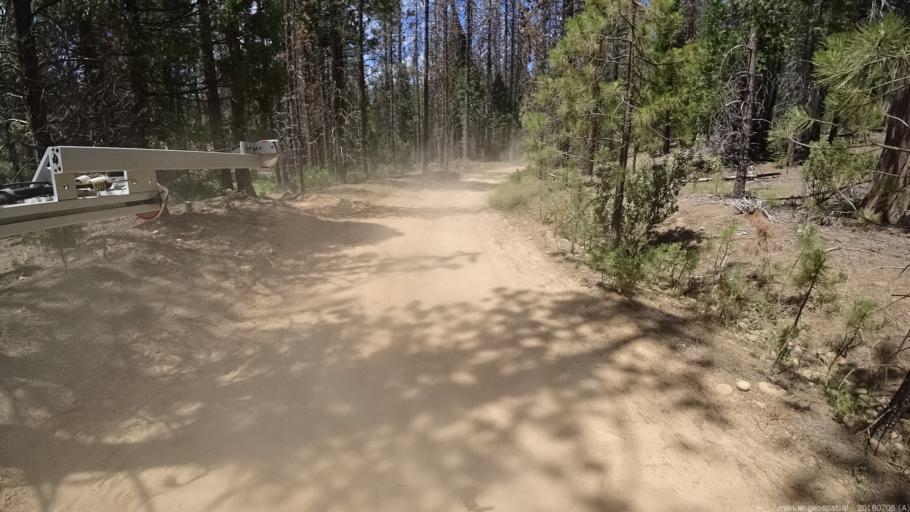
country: US
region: California
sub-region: Madera County
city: Oakhurst
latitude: 37.4165
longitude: -119.3777
